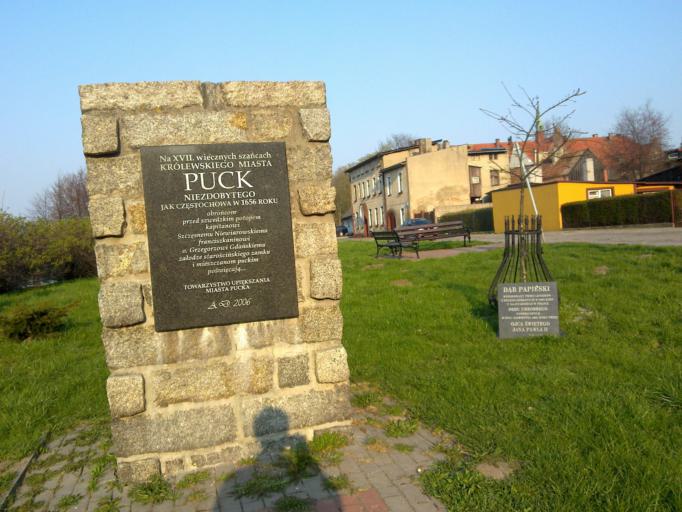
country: PL
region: Pomeranian Voivodeship
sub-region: Powiat pucki
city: Puck
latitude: 54.7220
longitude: 18.4118
